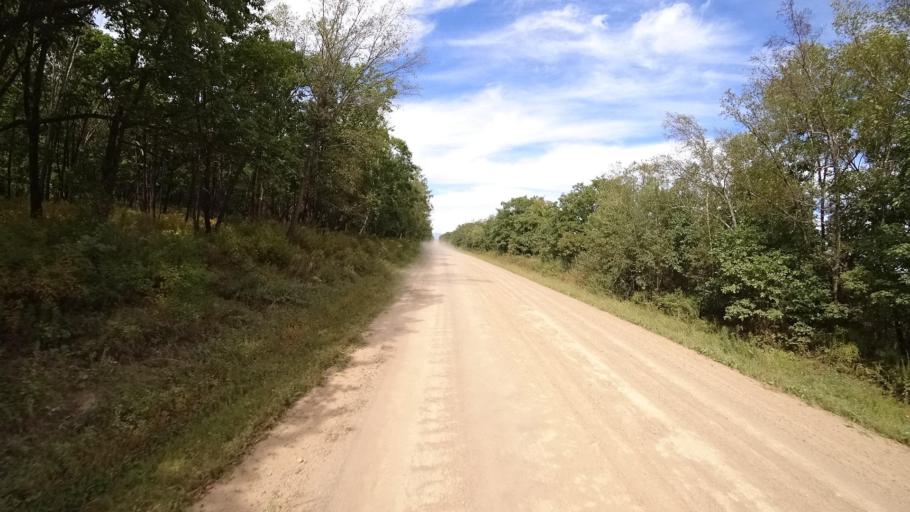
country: RU
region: Primorskiy
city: Yakovlevka
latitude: 44.5981
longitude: 133.6057
